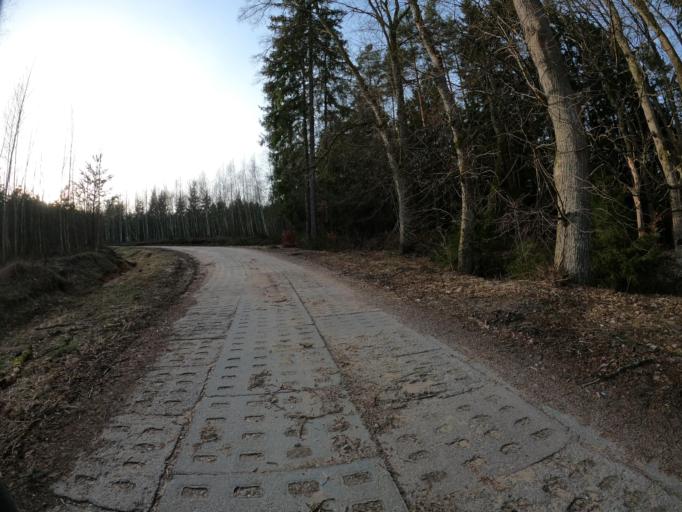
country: PL
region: West Pomeranian Voivodeship
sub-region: Powiat koszalinski
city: Polanow
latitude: 54.1451
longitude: 16.6744
